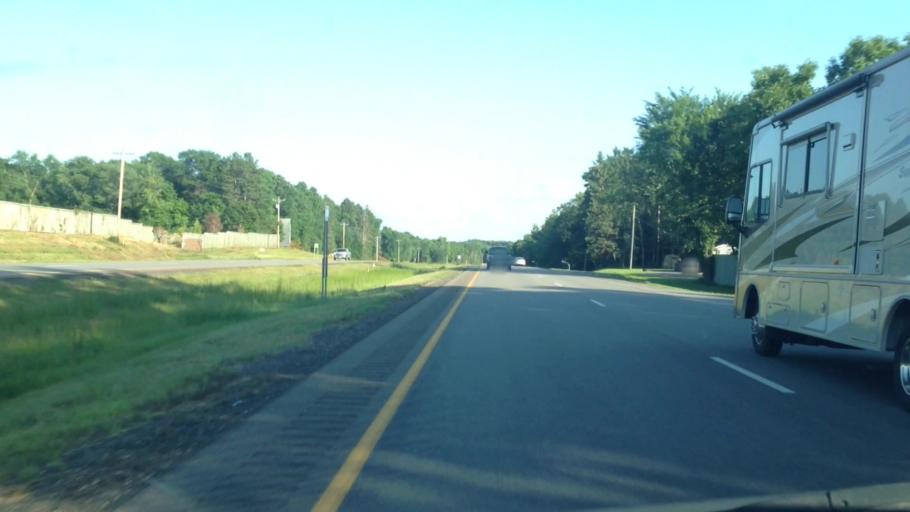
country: US
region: Minnesota
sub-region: Sherburne County
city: Zimmerman
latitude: 45.4255
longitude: -93.5709
